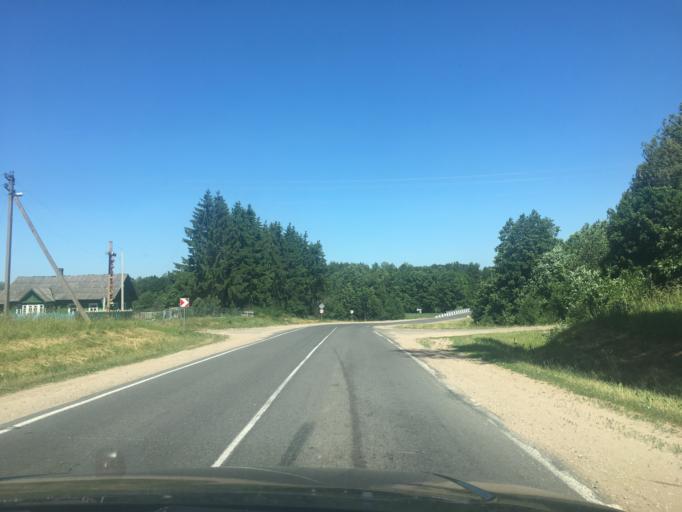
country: BY
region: Grodnenskaya
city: Hal'shany
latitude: 54.2130
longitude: 25.9652
